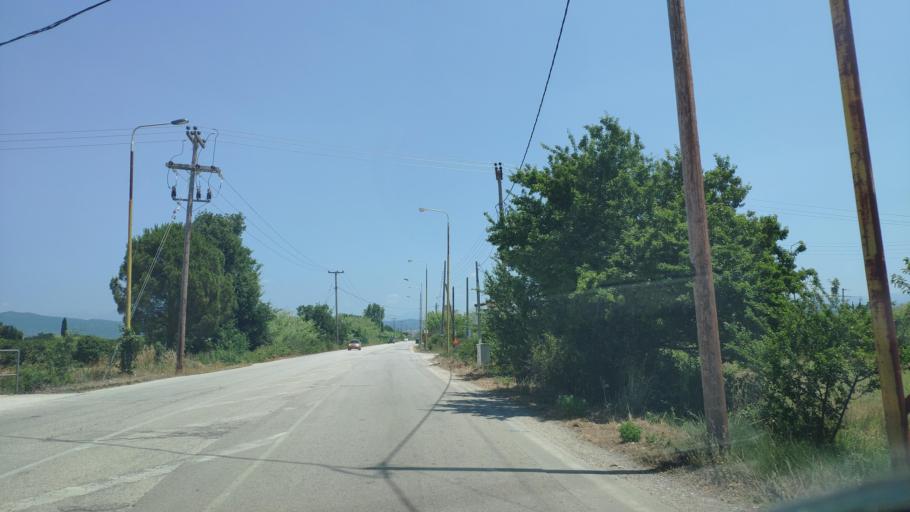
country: GR
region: Epirus
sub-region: Nomos Artas
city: Kostakioi
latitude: 39.1245
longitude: 20.9412
